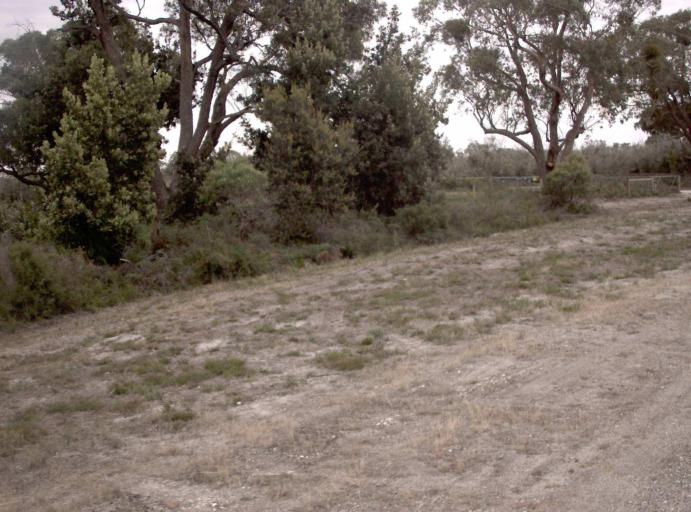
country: AU
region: Victoria
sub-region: Wellington
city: Sale
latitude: -38.1841
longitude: 147.3728
